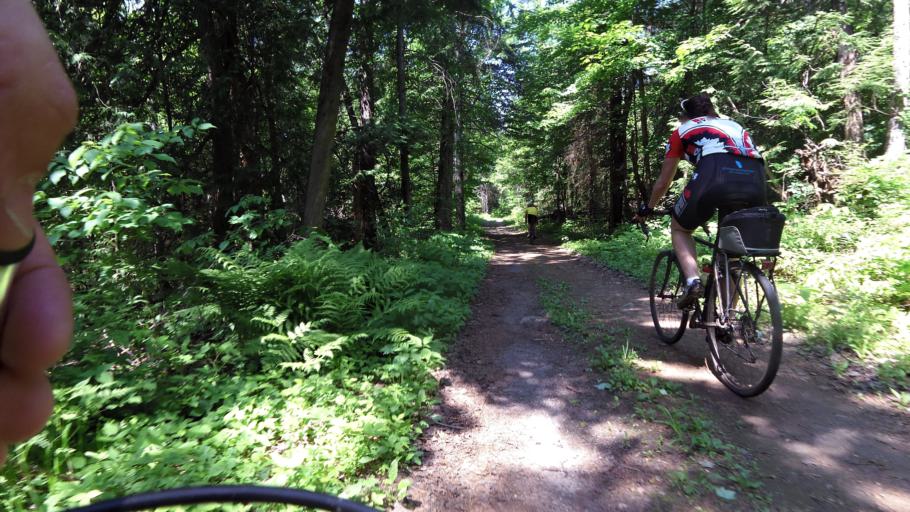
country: CA
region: Quebec
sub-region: Outaouais
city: Wakefield
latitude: 45.5677
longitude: -75.9137
